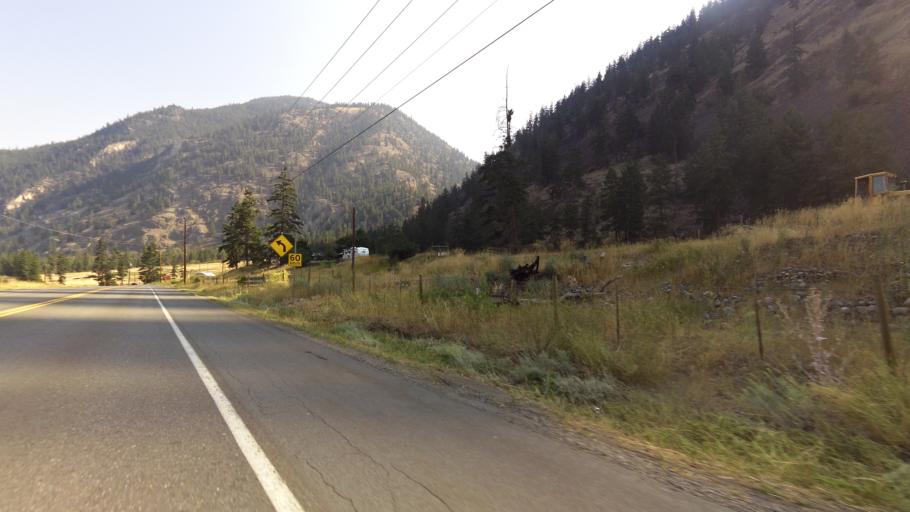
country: CA
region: British Columbia
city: Summerland
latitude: 49.3041
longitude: -120.0277
